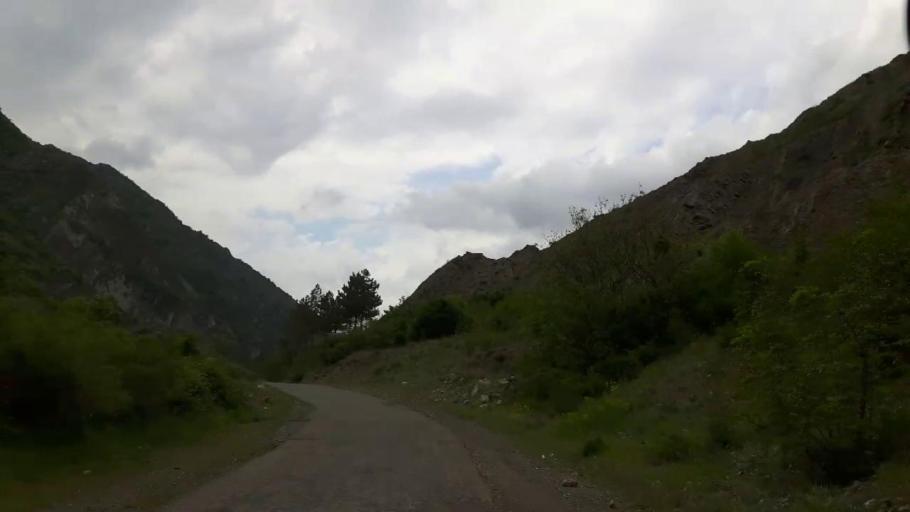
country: GE
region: Shida Kartli
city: Gori
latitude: 41.9008
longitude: 44.0841
